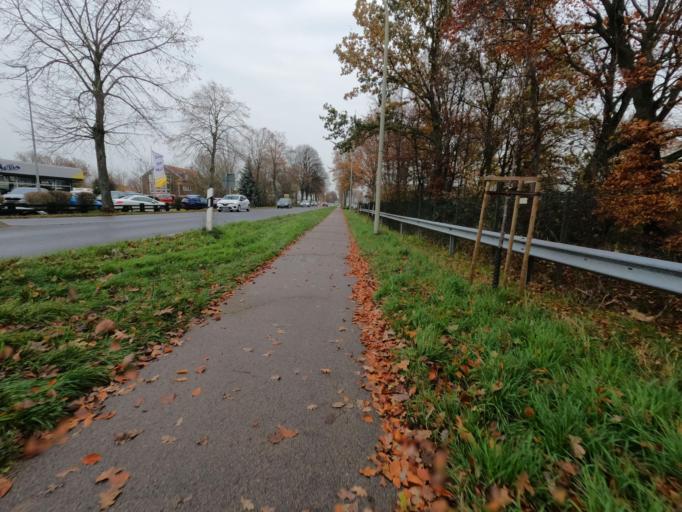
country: DE
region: North Rhine-Westphalia
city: Geilenkirchen
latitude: 50.9820
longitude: 6.1195
